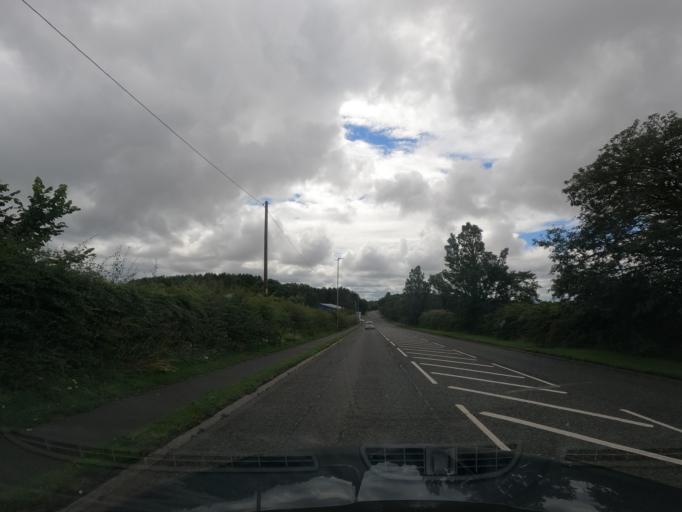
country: GB
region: England
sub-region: Northumberland
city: Berwick-Upon-Tweed
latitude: 55.7460
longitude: -1.9981
